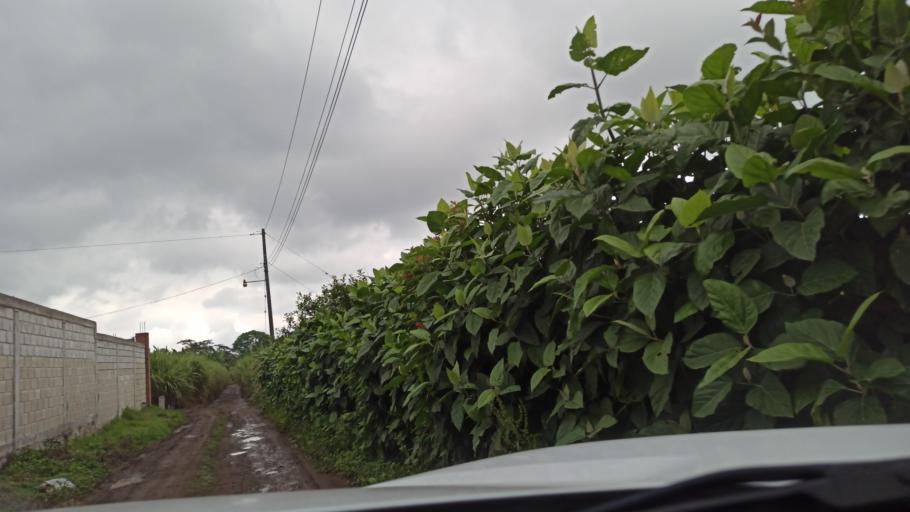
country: MX
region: Veracruz
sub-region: Fortin
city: Santa Lucia Potrerillo
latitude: 18.9704
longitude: -97.0271
